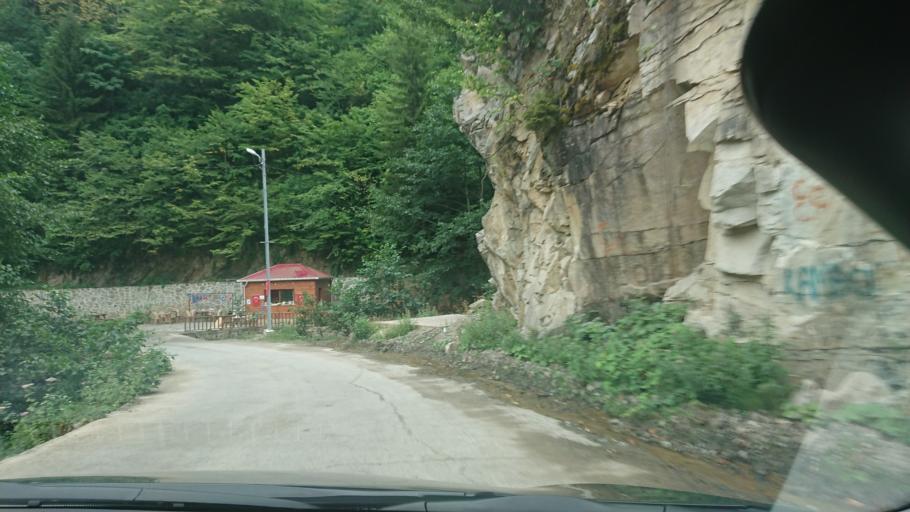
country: TR
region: Gumushane
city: Kurtun
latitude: 40.6855
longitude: 39.0520
